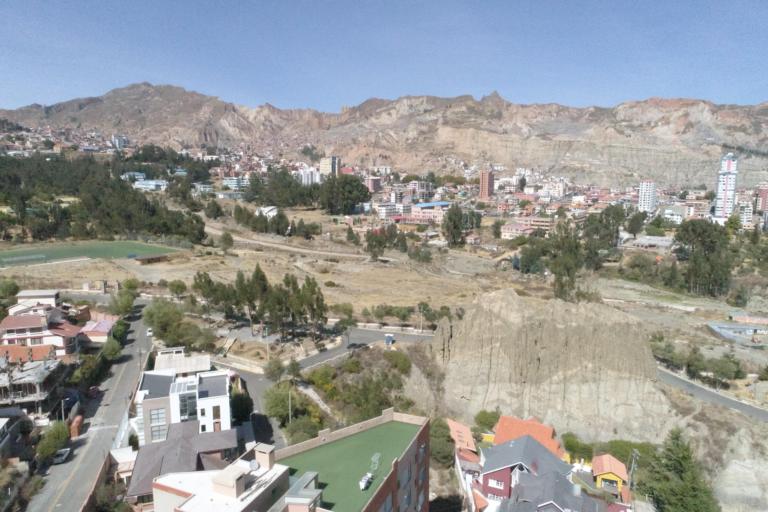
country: BO
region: La Paz
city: La Paz
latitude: -16.5342
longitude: -68.0689
